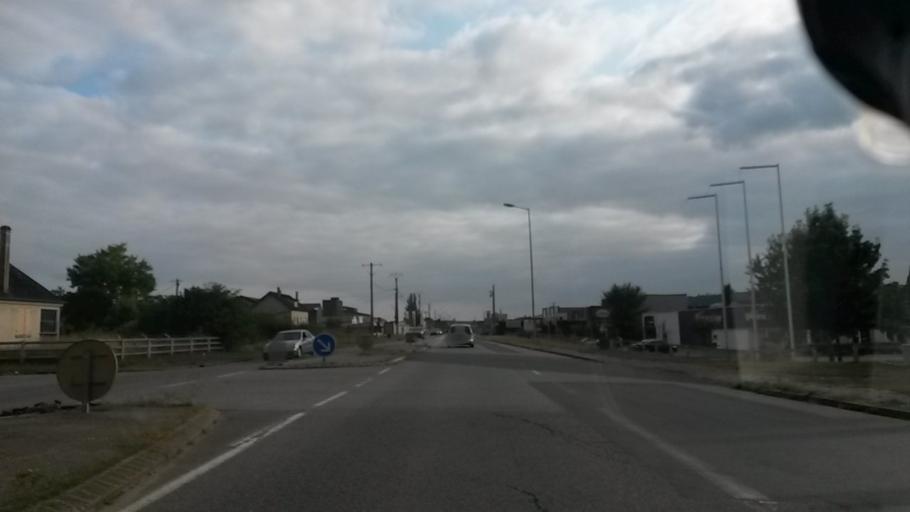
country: FR
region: Haute-Normandie
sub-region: Departement de l'Eure
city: Gravigny
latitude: 49.0590
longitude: 1.1695
